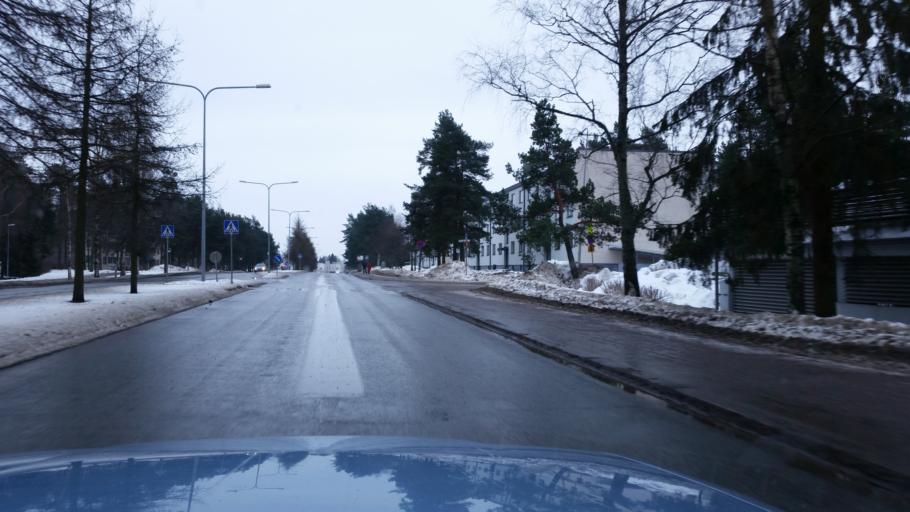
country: FI
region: Uusimaa
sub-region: Helsinki
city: Vantaa
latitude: 60.2388
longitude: 25.0760
